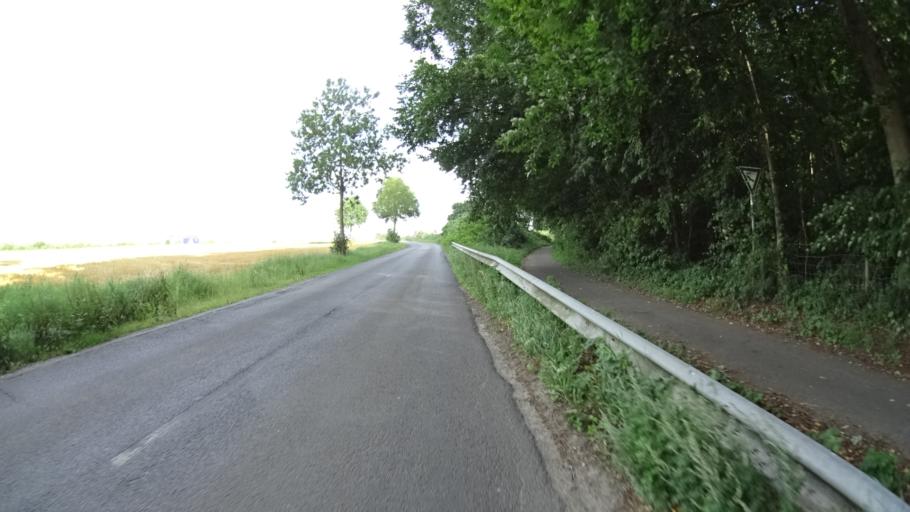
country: DE
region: Lower Saxony
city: Reppenstedt
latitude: 53.2375
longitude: 10.3757
